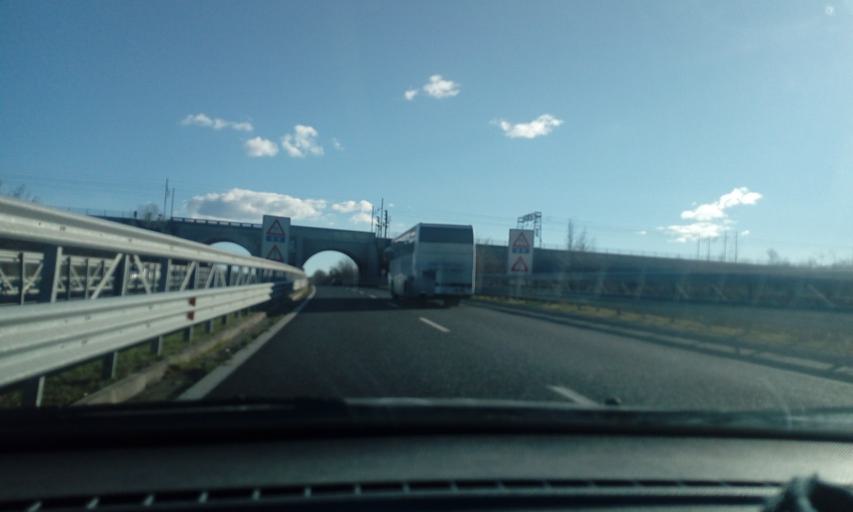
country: IT
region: Friuli Venezia Giulia
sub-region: Provincia di Trieste
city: Sistiana-Visogliano
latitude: 45.7659
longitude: 13.6511
